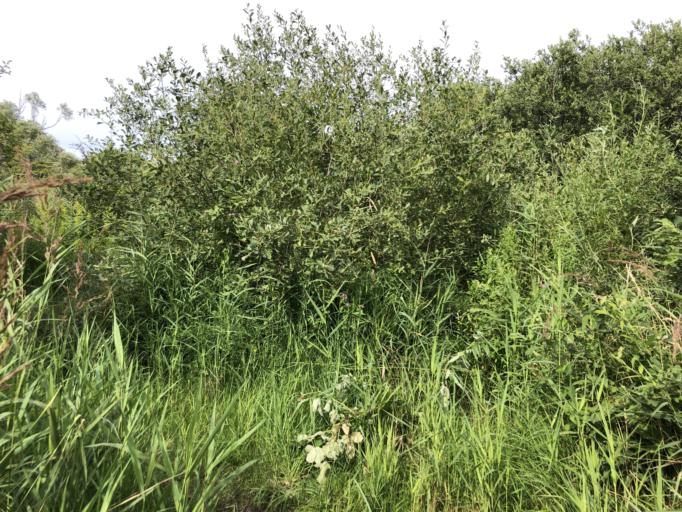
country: DK
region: Capital Region
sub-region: Kobenhavn
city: Christianshavn
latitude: 55.6551
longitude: 12.5796
